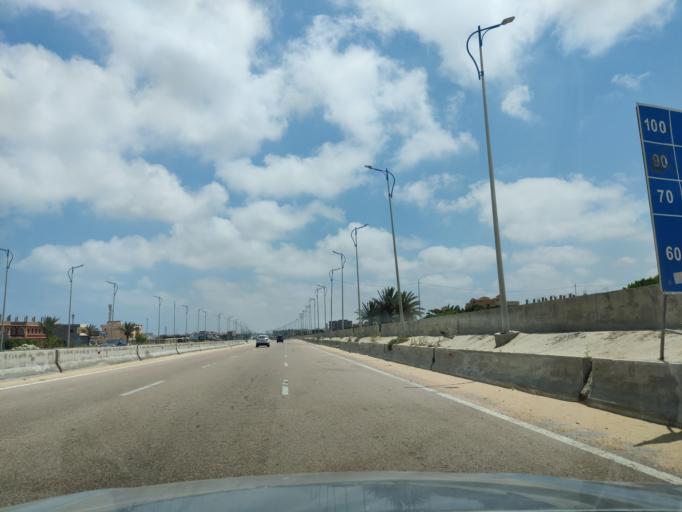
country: EG
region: Alexandria
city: Alexandria
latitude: 30.9734
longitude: 29.5676
